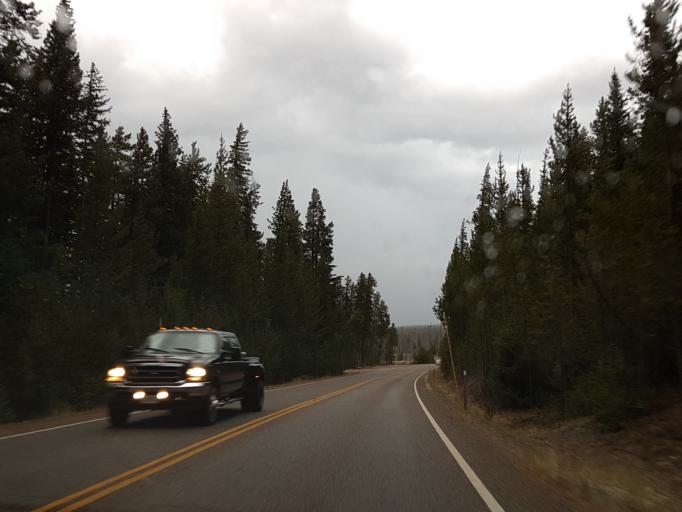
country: US
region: Montana
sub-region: Gallatin County
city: West Yellowstone
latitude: 44.4653
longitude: -110.5160
